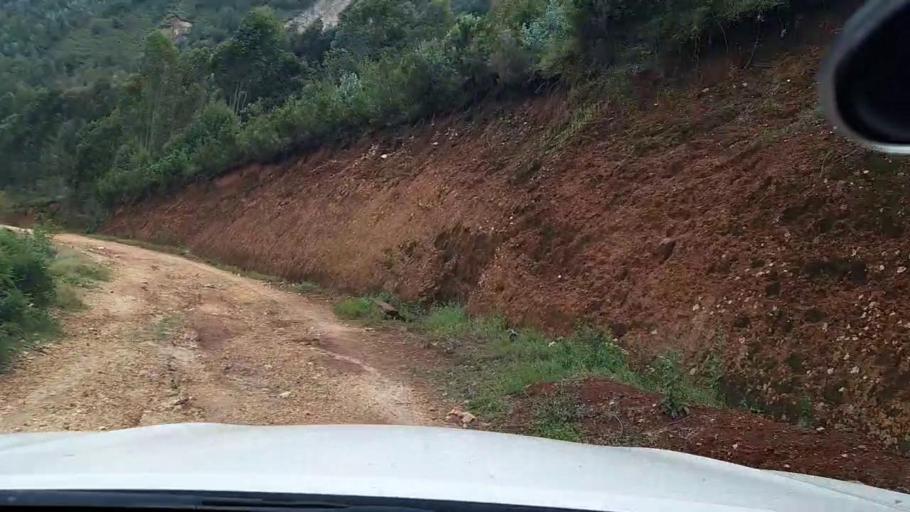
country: RW
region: Western Province
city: Kibuye
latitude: -2.1609
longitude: 29.4530
